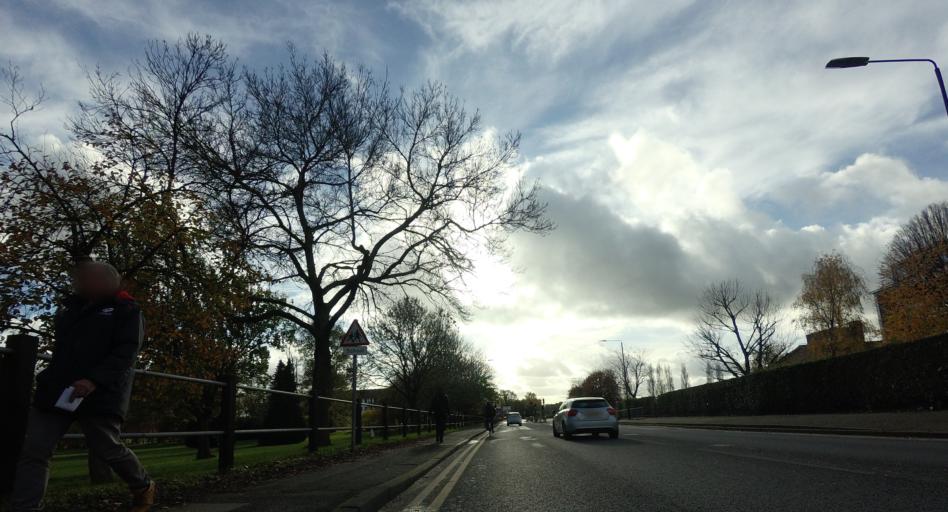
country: GB
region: England
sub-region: Greater London
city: Sidcup
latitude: 51.4213
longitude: 0.0996
